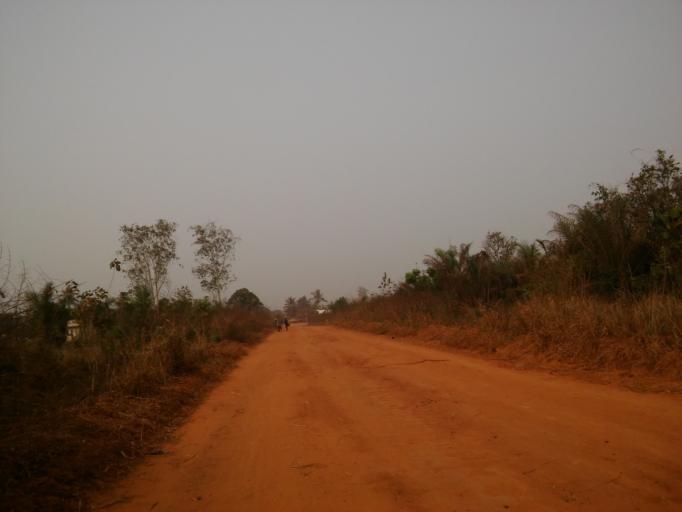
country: BJ
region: Kouffo
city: Dogbo
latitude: 6.7821
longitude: 1.7755
